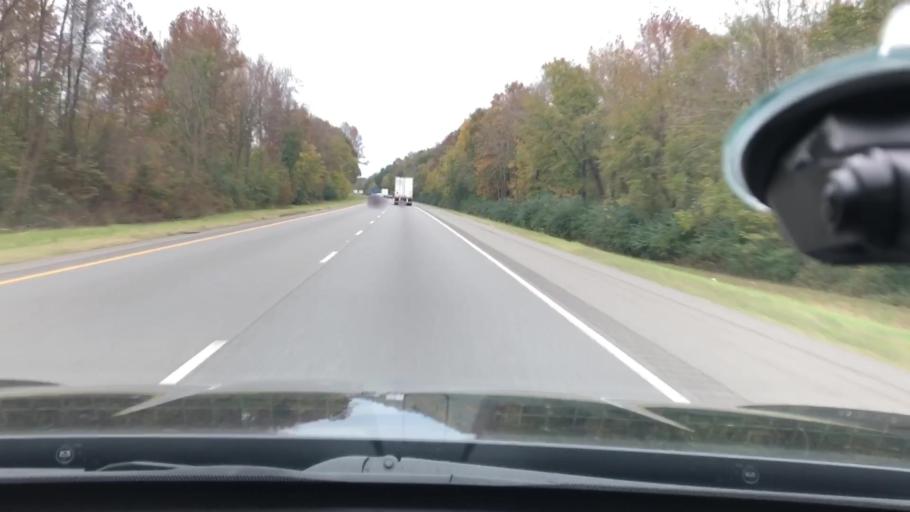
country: US
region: Arkansas
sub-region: Hempstead County
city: Hope
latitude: 33.6601
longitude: -93.6443
